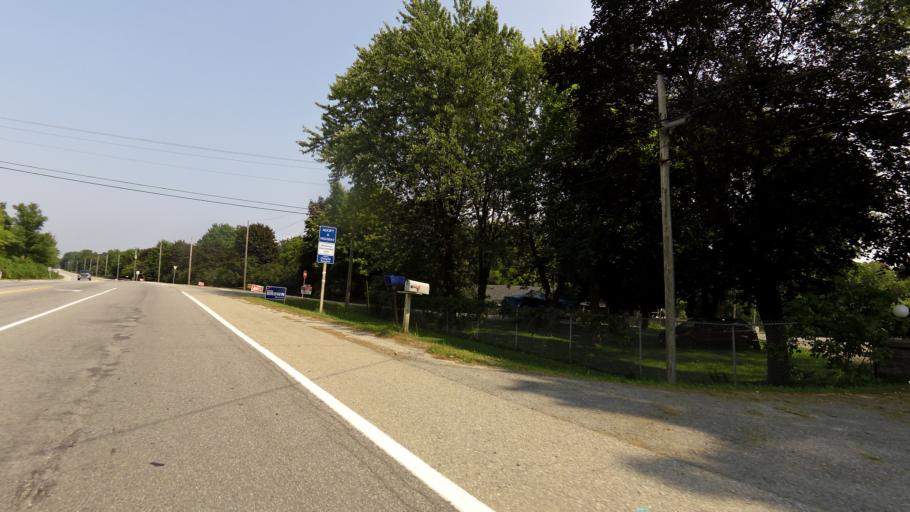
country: CA
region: Ontario
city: Brockville
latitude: 44.6107
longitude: -75.6522
